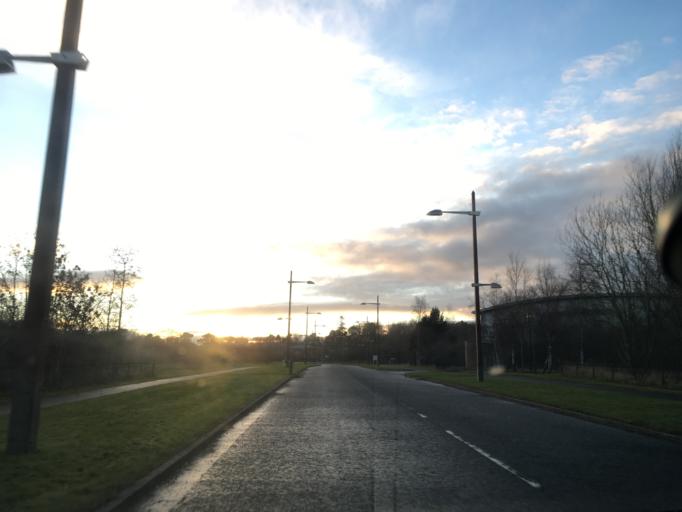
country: GB
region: Scotland
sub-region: Midlothian
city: Loanhead
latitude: 55.8608
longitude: -3.1890
